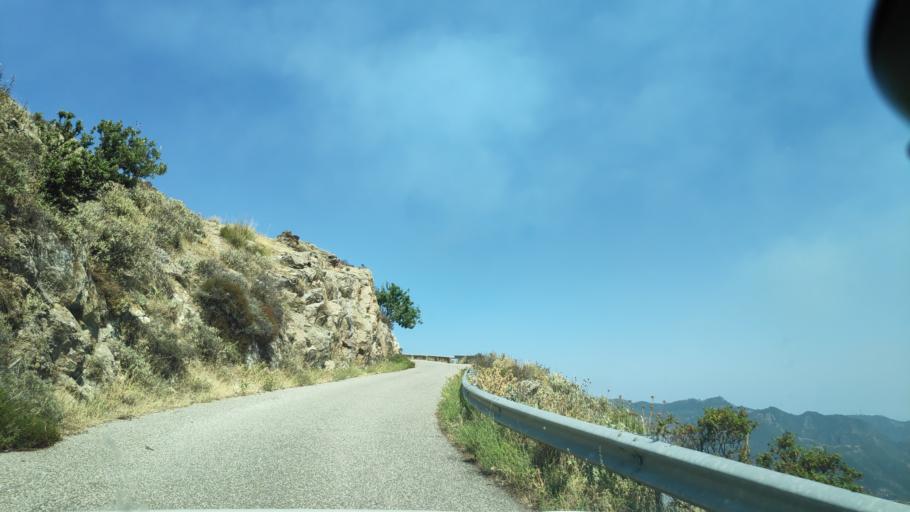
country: IT
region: Calabria
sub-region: Provincia di Reggio Calabria
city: Bova
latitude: 38.0052
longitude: 15.9304
